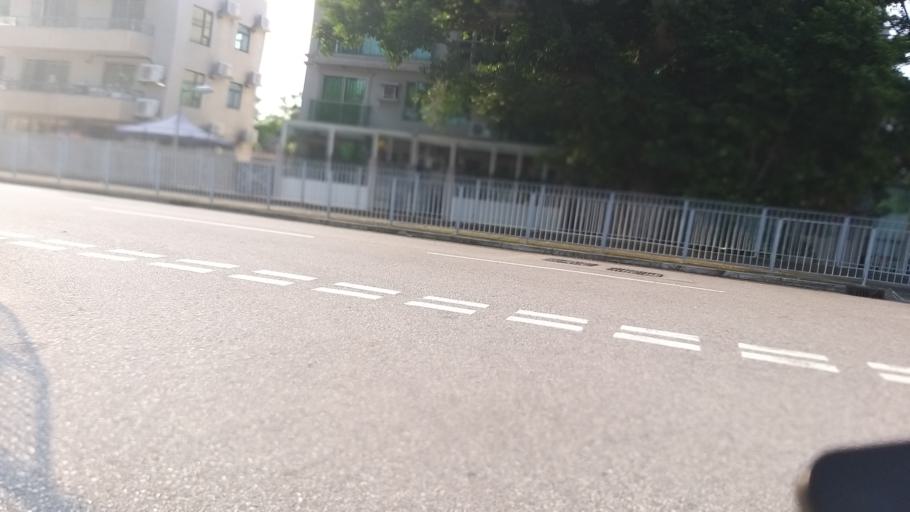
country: HK
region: Yuen Long
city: Yuen Long Kau Hui
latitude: 22.4514
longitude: 114.0338
